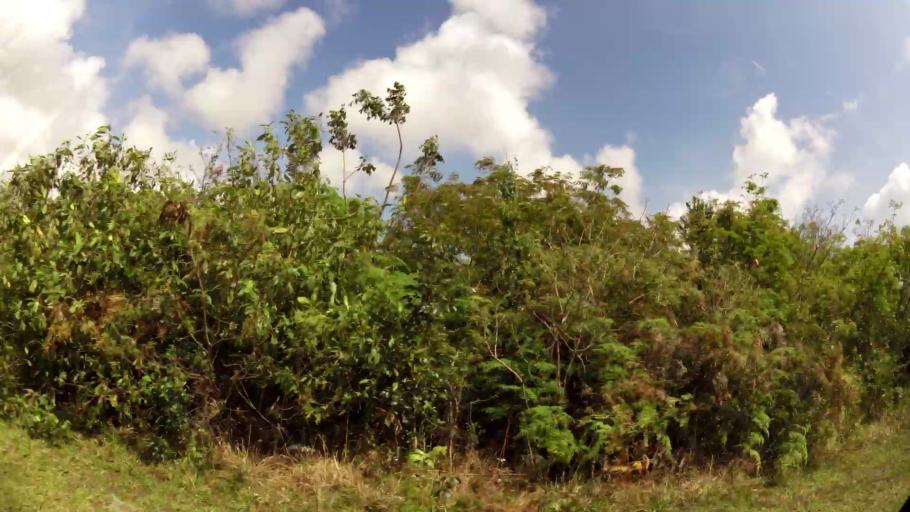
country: BS
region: Freeport
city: Freeport
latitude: 26.5118
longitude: -78.7145
